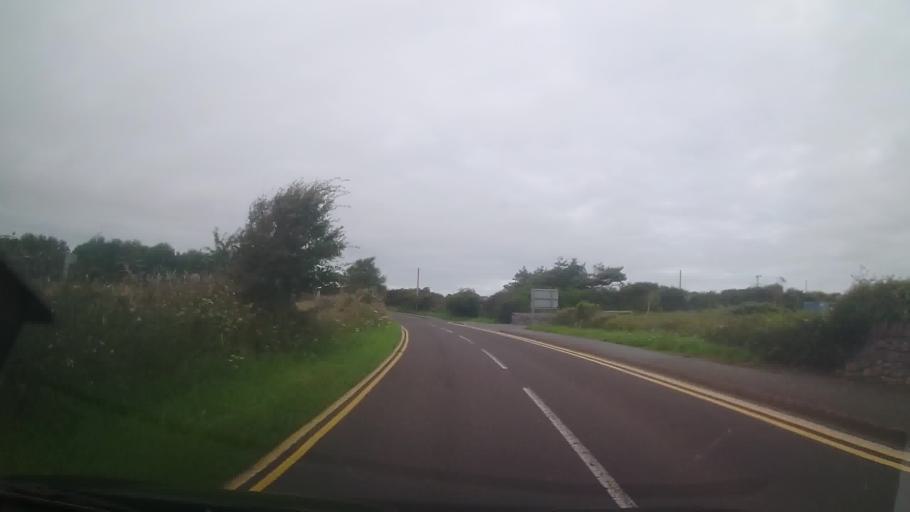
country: GB
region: Wales
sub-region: Gwynedd
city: Caernarfon
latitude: 53.1607
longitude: -4.3512
